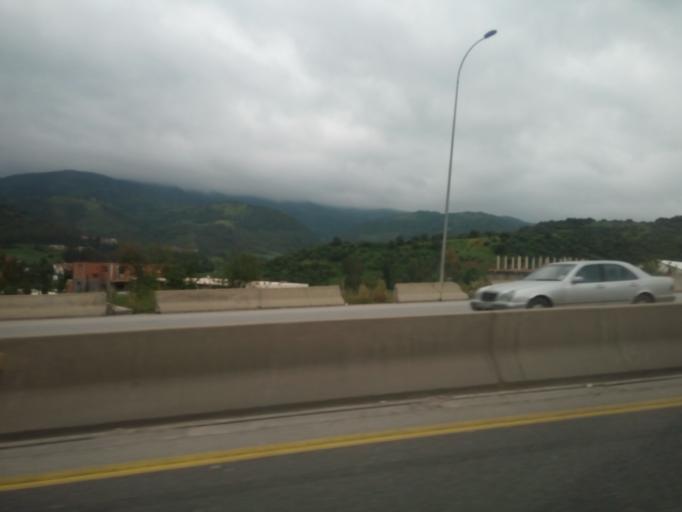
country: DZ
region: Bouira
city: Lakhdaria
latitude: 36.5773
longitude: 3.5572
